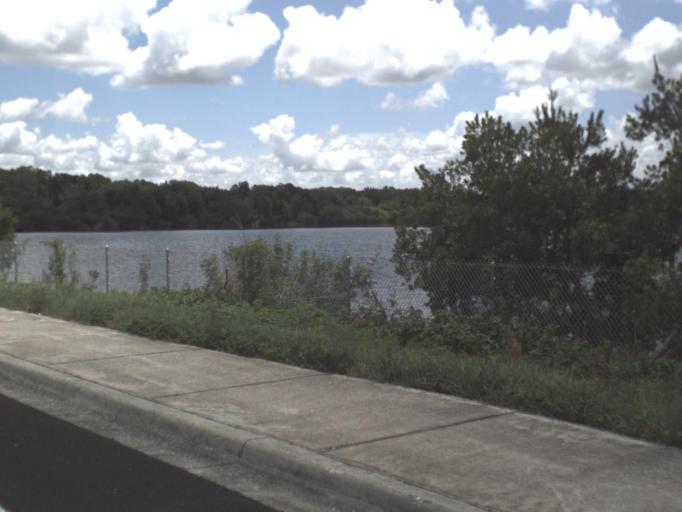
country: US
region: Florida
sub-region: Hillsborough County
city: Mango
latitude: 27.9813
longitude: -82.3174
